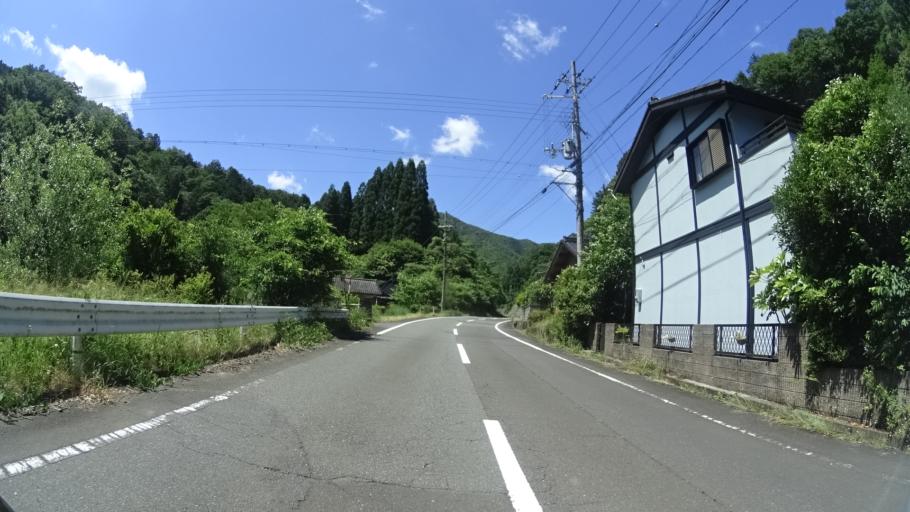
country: JP
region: Kyoto
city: Miyazu
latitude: 35.4163
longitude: 135.1862
